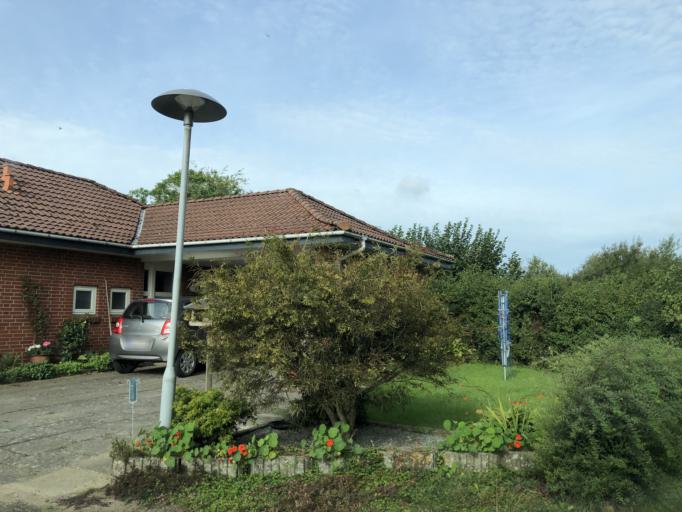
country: DK
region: South Denmark
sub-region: Vejle Kommune
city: Borkop
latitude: 55.6040
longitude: 9.6549
